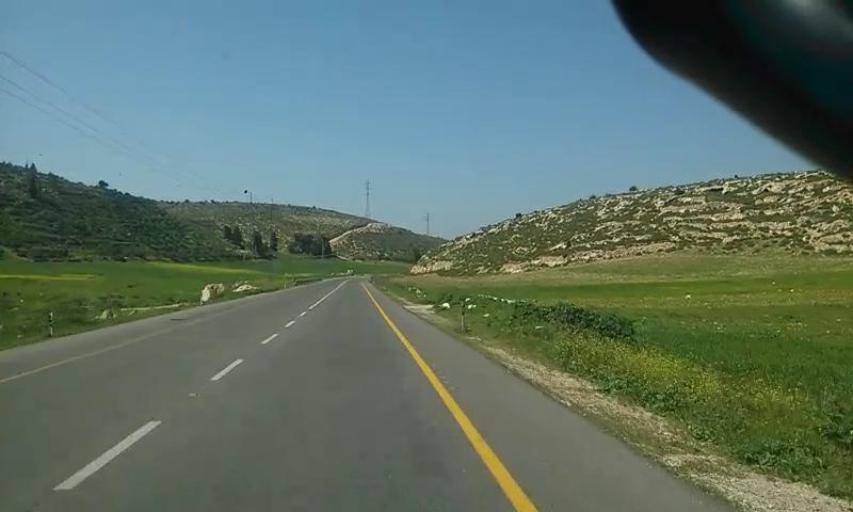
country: PS
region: West Bank
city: Idhna
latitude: 31.5814
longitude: 34.9752
